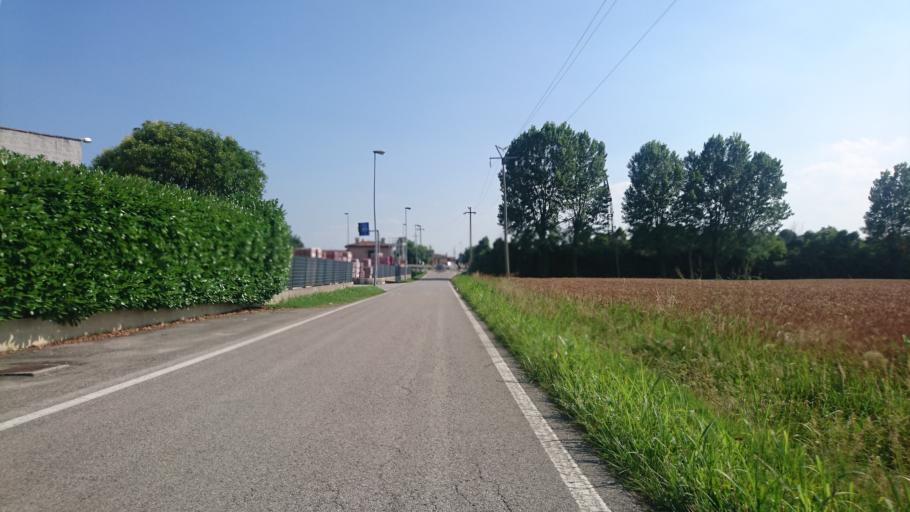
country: IT
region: Veneto
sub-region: Provincia di Venezia
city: Fornase
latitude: 45.4368
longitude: 12.1934
